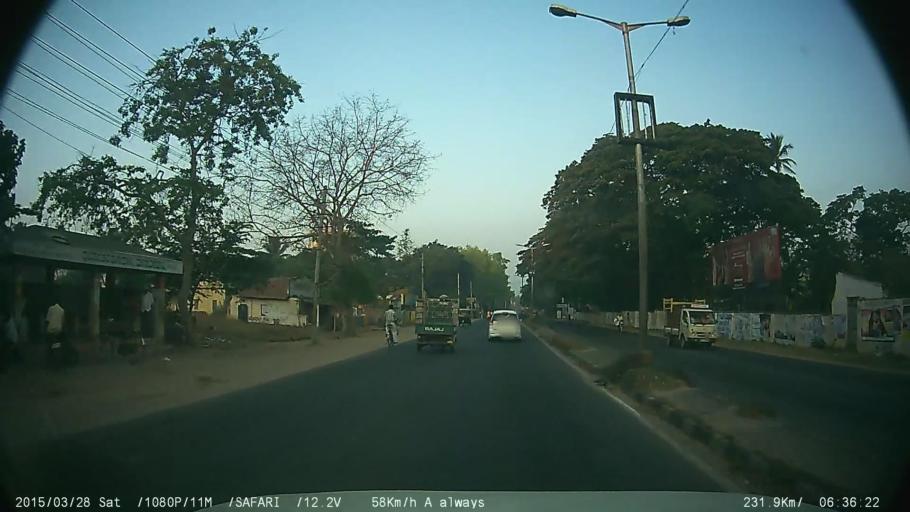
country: IN
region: Karnataka
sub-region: Ramanagara
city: Channapatna
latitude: 12.6505
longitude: 77.1945
